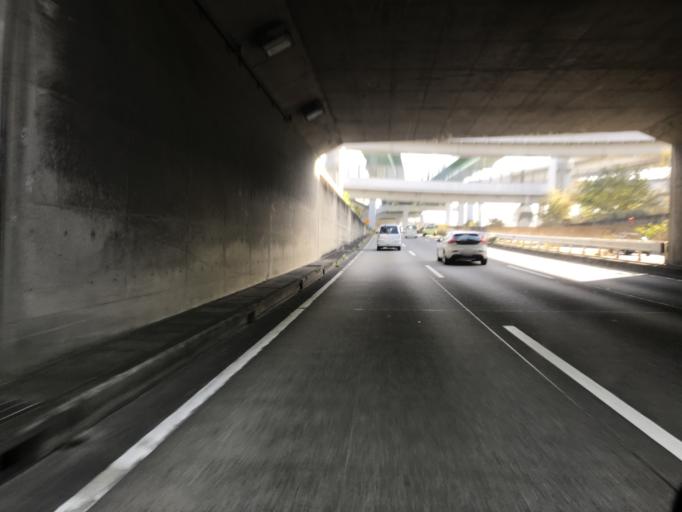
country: JP
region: Aichi
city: Iwakura
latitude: 35.2215
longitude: 136.8551
